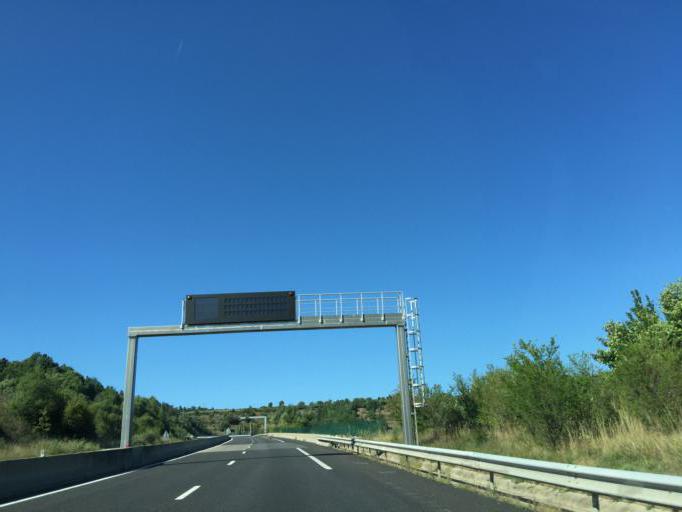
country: FR
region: Languedoc-Roussillon
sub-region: Departement de la Lozere
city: La Canourgue
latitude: 44.4742
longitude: 3.1984
